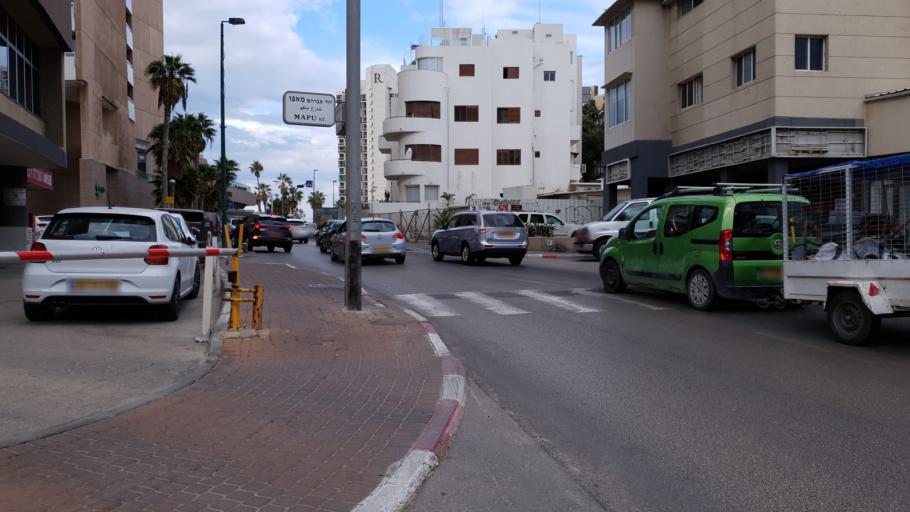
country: IL
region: Tel Aviv
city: Tel Aviv
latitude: 32.0806
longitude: 34.7684
